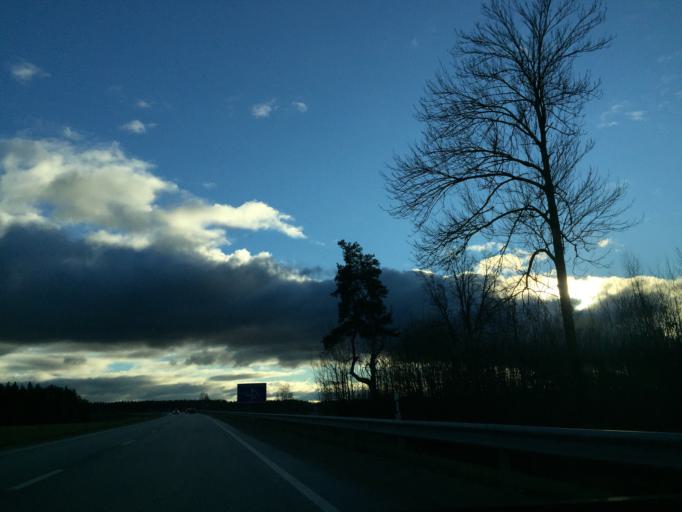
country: LV
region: Koceni
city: Koceni
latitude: 57.5307
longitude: 25.3700
